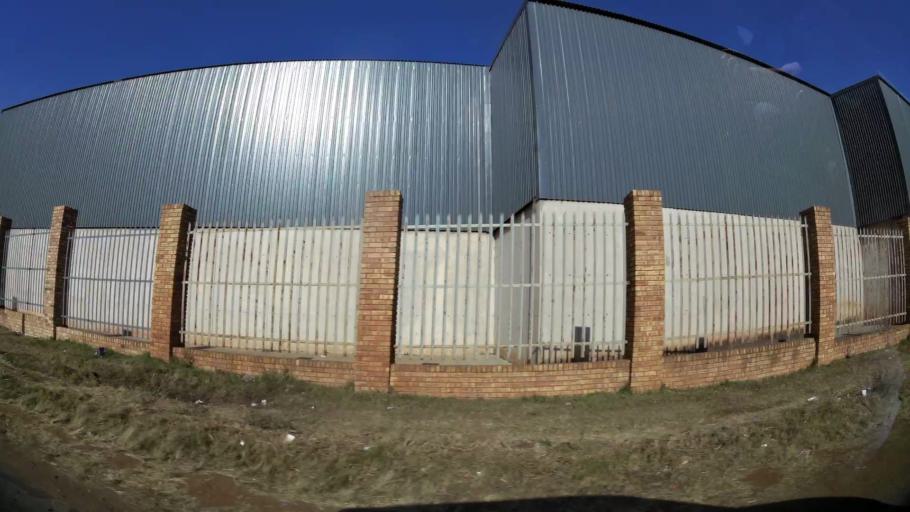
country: ZA
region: Gauteng
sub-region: West Rand District Municipality
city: Randfontein
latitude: -26.1621
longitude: 27.7110
